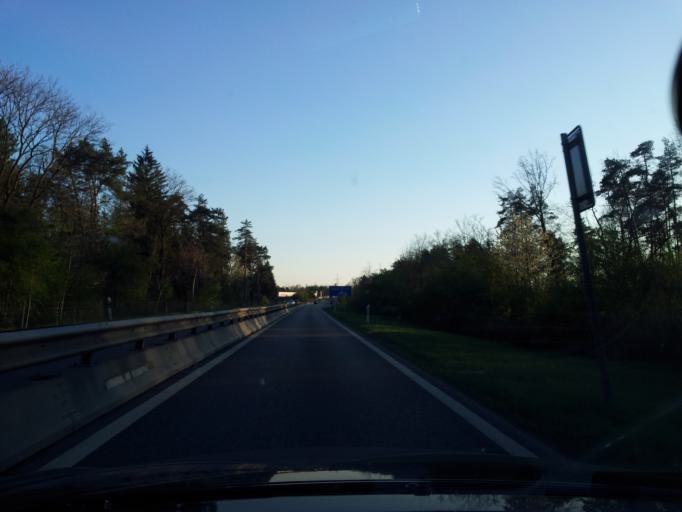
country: CH
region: Bern
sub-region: Seeland District
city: Lyss
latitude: 47.0867
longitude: 7.3007
